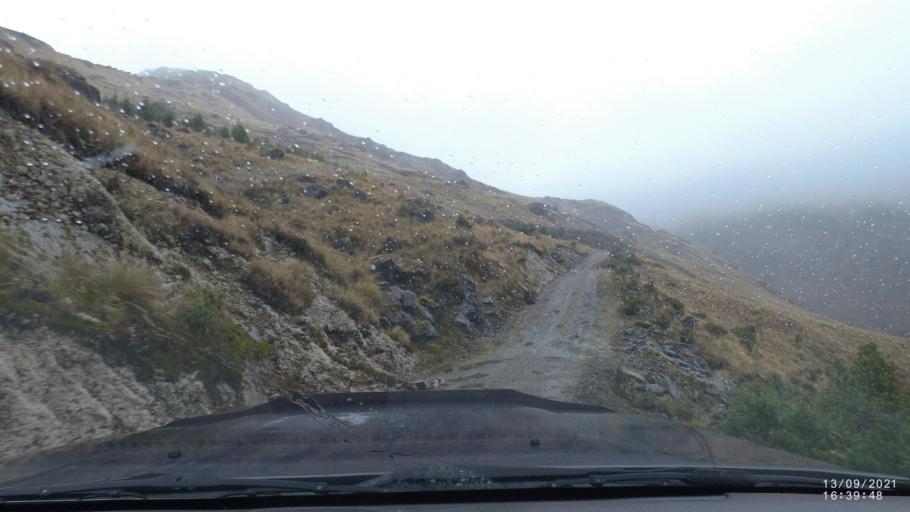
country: BO
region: Cochabamba
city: Colomi
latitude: -17.2799
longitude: -65.7093
